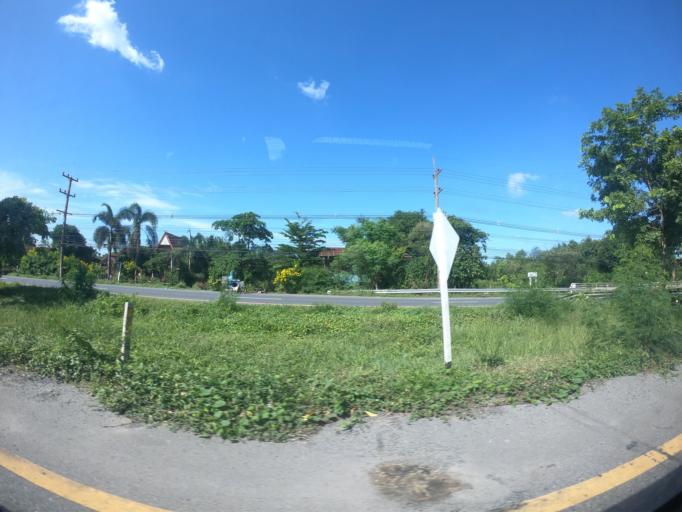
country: TH
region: Nakhon Nayok
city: Ban Na
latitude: 14.2515
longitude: 101.0974
